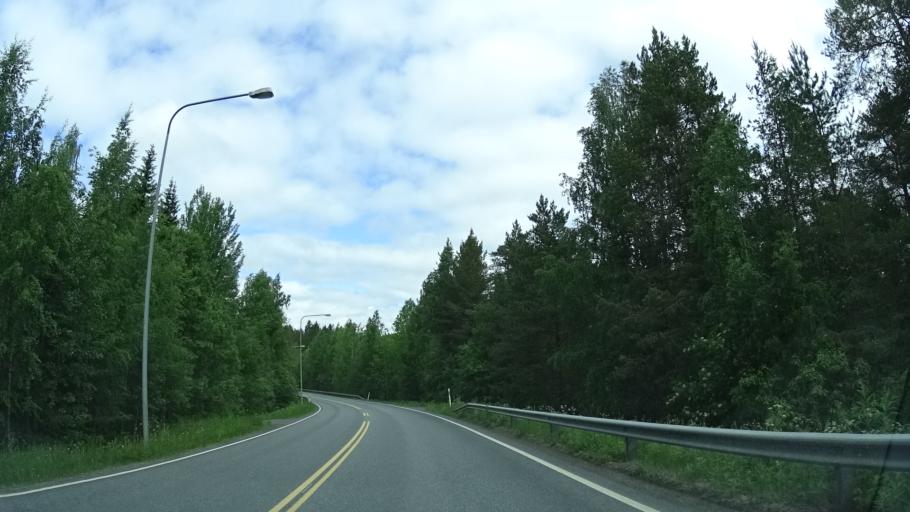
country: FI
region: Central Finland
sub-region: Jyvaeskylae
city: Korpilahti
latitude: 62.0028
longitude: 25.6799
